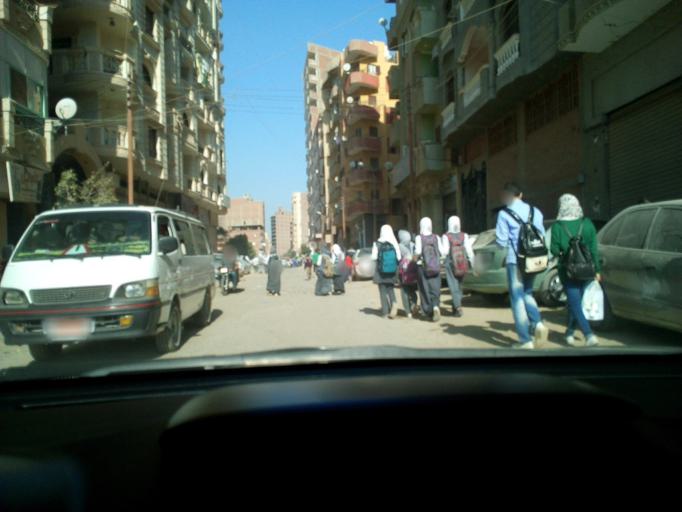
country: EG
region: Muhafazat al Fayyum
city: Al Fayyum
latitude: 29.3264
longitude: 30.8374
